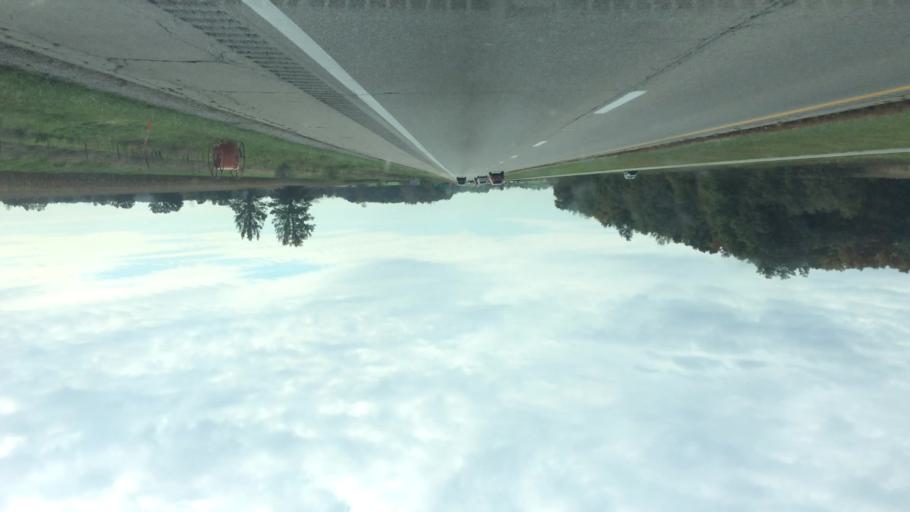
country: US
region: Ohio
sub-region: Union County
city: New California
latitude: 40.1800
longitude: -83.2490
